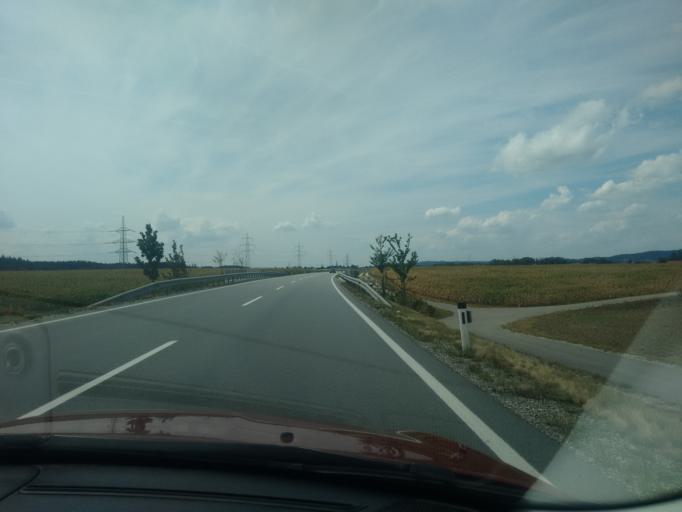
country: DE
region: Bavaria
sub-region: Lower Bavaria
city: Ering
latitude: 48.2553
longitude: 13.1284
